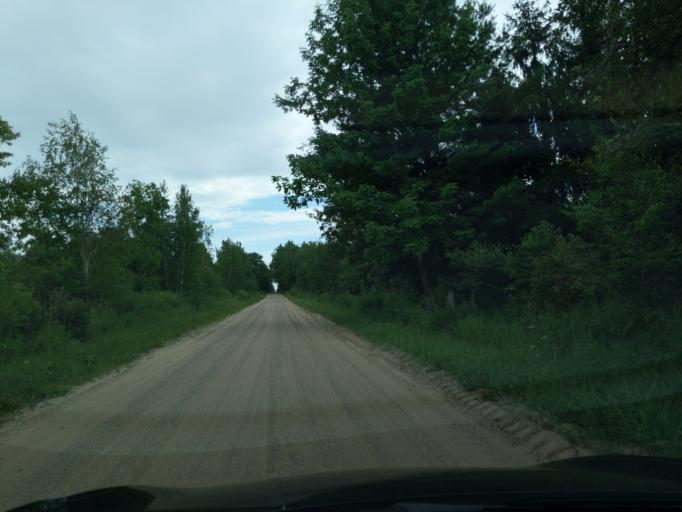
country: US
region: Michigan
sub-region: Clare County
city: Harrison
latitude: 43.9943
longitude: -85.0083
